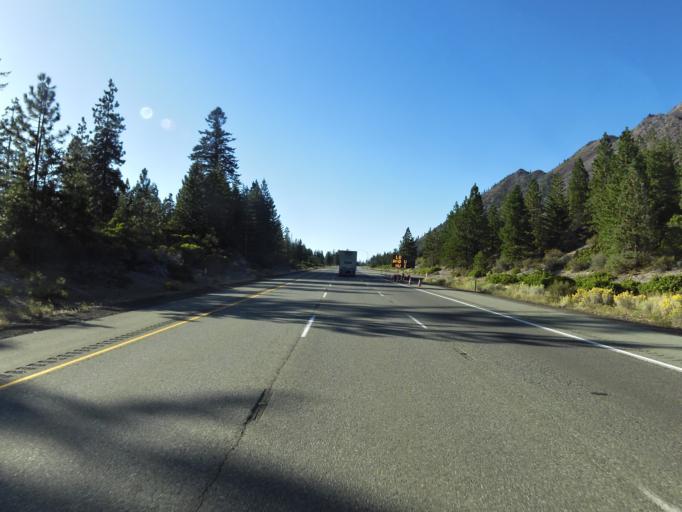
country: US
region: California
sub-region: Siskiyou County
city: Mount Shasta
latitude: 41.3460
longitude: -122.3447
